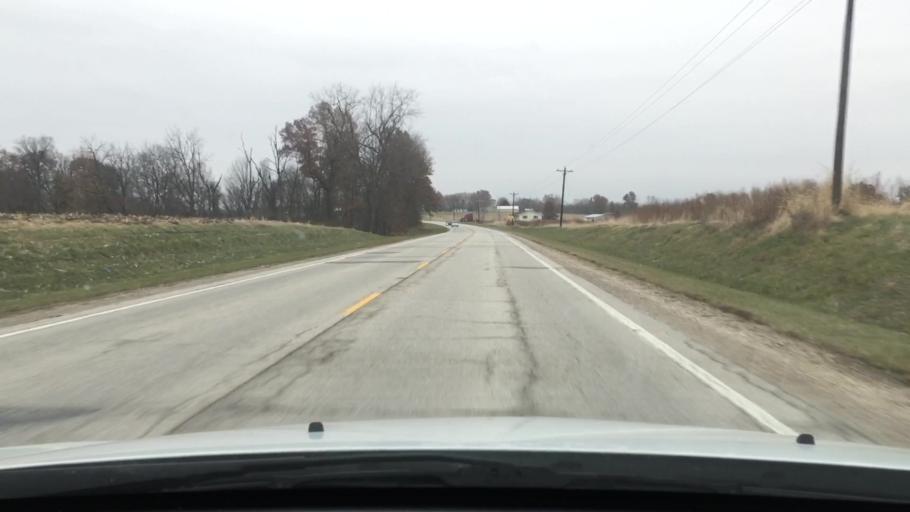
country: US
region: Illinois
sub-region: Pike County
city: Pittsfield
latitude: 39.5669
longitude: -90.9150
